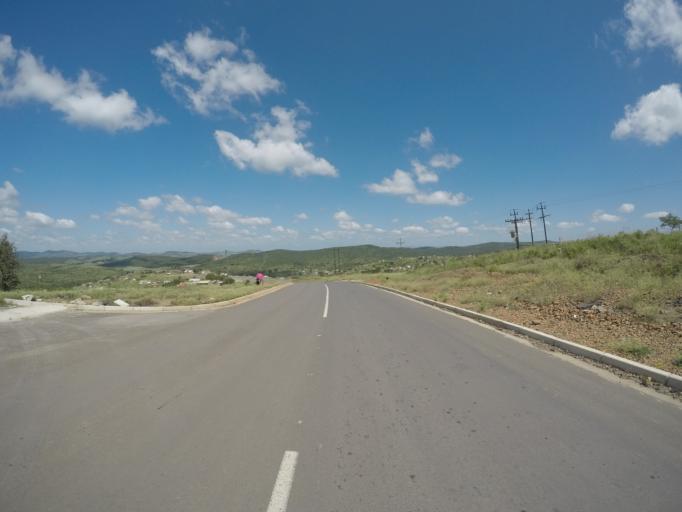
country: ZA
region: KwaZulu-Natal
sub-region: uThungulu District Municipality
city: Empangeni
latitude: -28.6091
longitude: 31.7466
